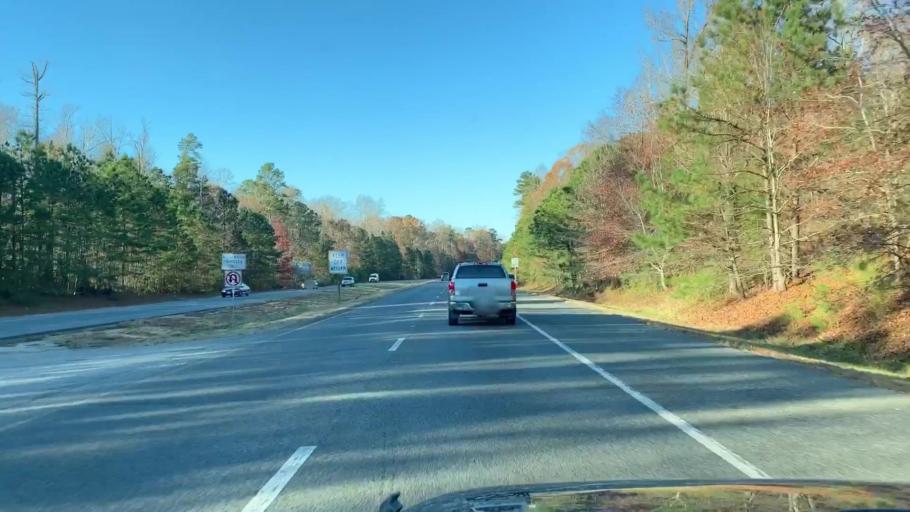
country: US
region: Virginia
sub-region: James City County
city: Williamsburg
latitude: 37.3133
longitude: -76.7482
